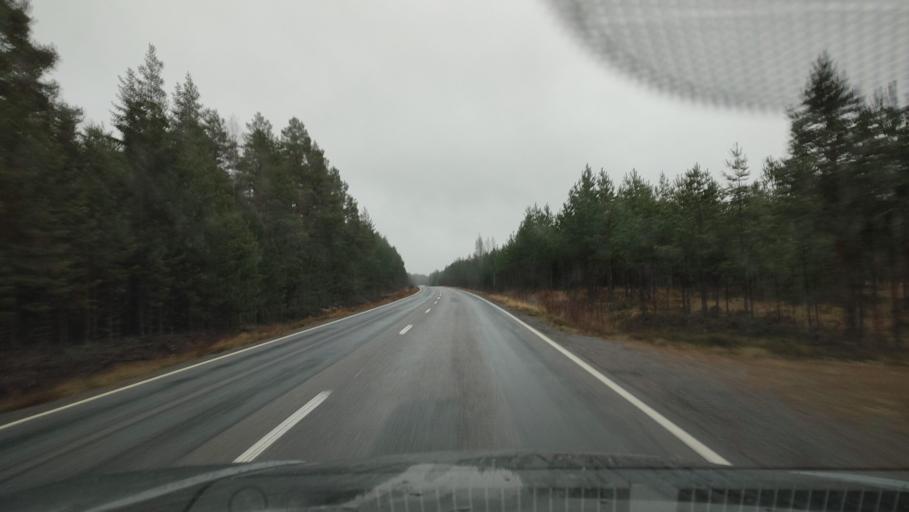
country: FI
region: Southern Ostrobothnia
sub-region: Suupohja
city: Karijoki
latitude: 62.2335
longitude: 21.7107
